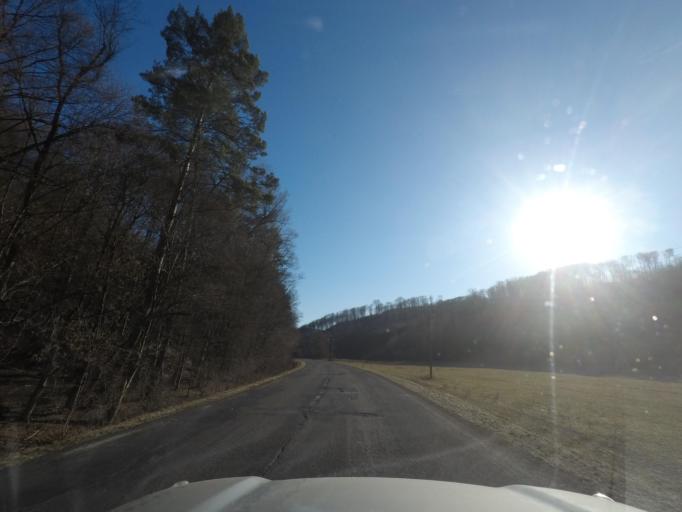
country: SK
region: Presovsky
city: Medzilaborce
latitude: 49.2721
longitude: 21.8011
